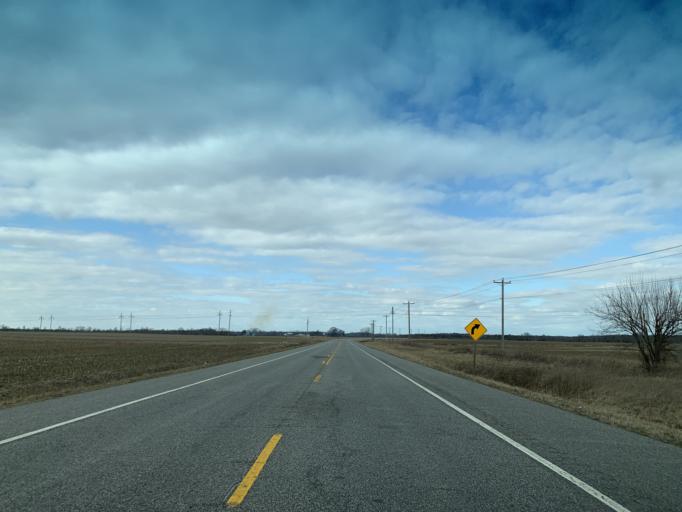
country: US
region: Maryland
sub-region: Queen Anne's County
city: Centreville
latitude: 38.9616
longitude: -76.0780
